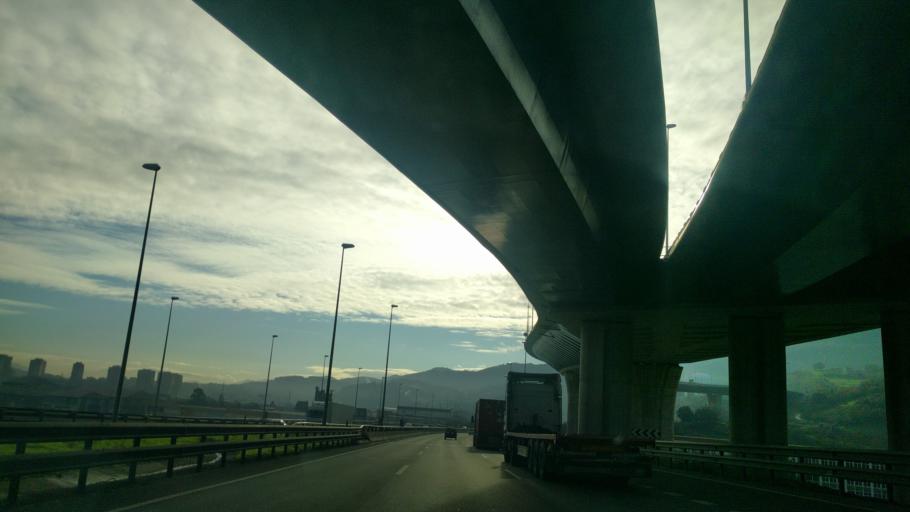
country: ES
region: Basque Country
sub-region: Bizkaia
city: Sestao
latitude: 43.3011
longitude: -3.0233
